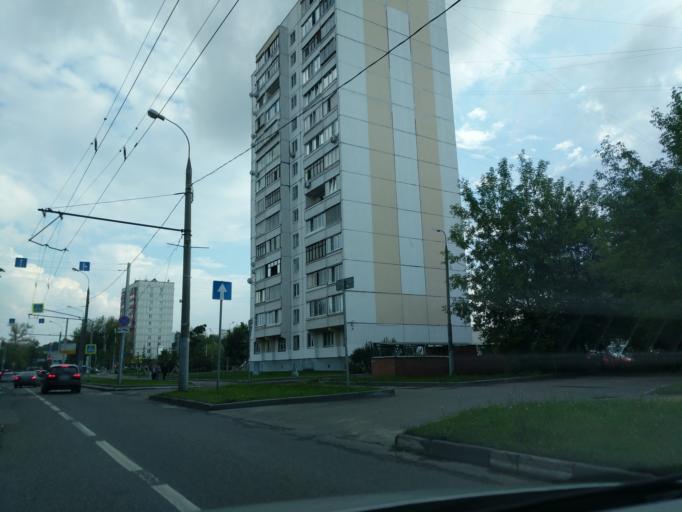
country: RU
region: Moscow
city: Gol'yanovo
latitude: 55.8143
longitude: 37.8284
